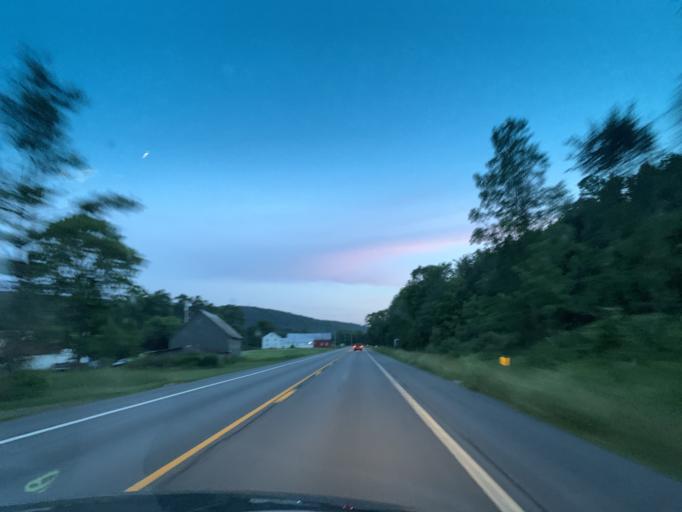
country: US
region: New York
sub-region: Chenango County
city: New Berlin
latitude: 42.5709
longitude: -75.3402
